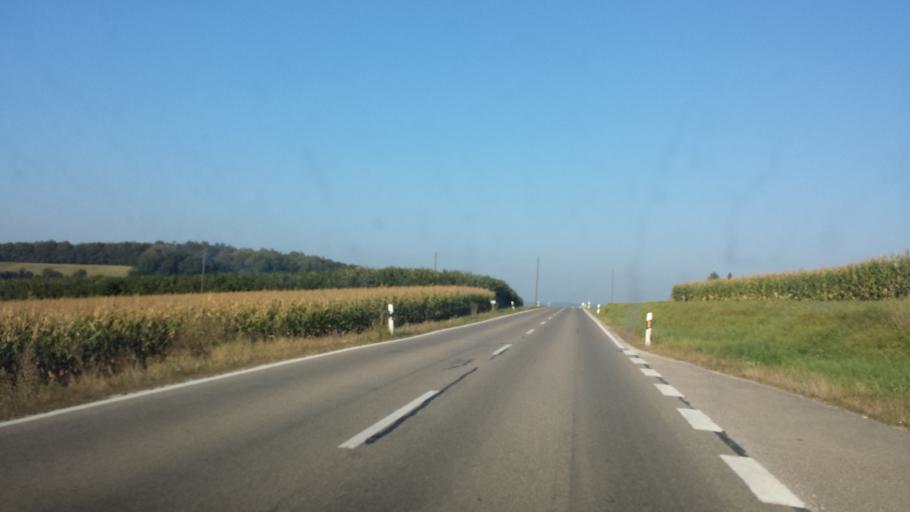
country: DE
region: Bavaria
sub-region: Upper Bavaria
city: Oberhausen
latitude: 48.7480
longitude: 11.1018
